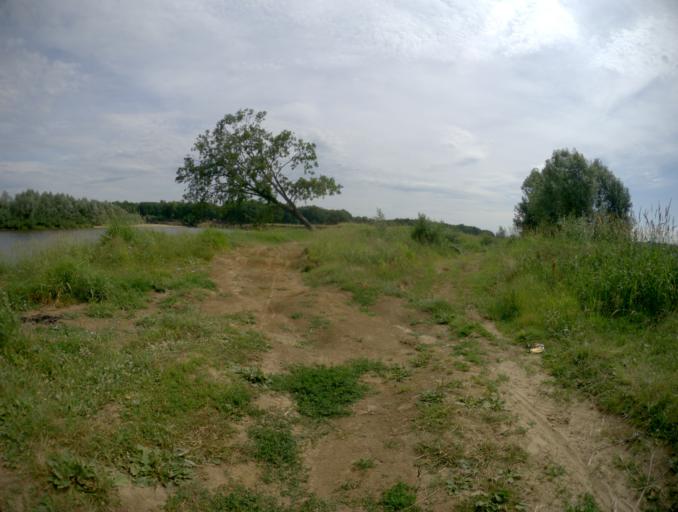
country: RU
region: Vladimir
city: Raduzhnyy
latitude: 56.0329
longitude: 40.2752
